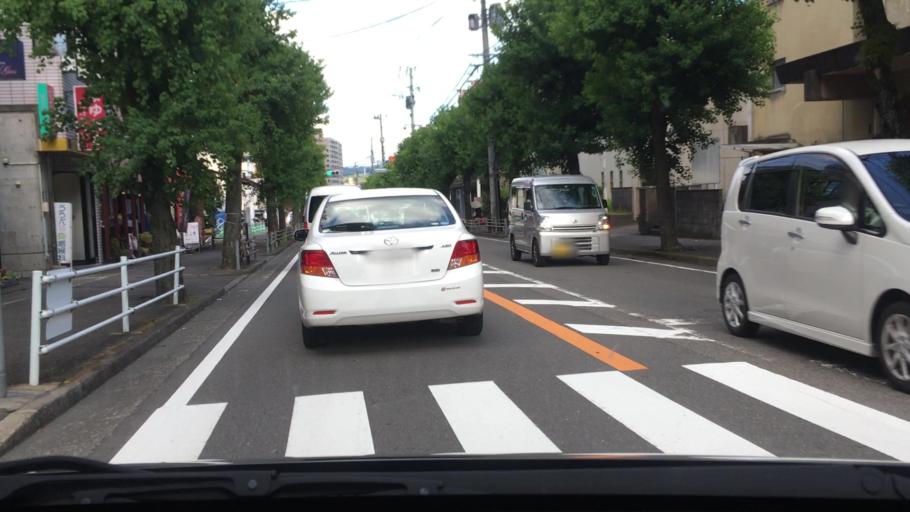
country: JP
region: Nagasaki
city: Togitsu
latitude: 32.8077
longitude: 129.8357
